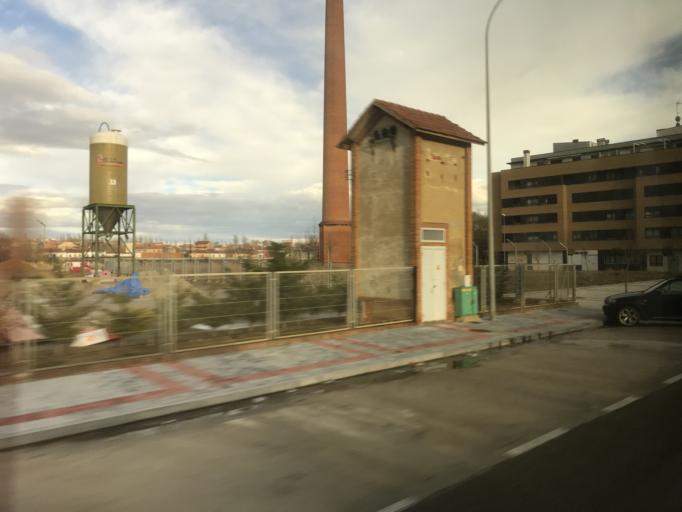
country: ES
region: Castille and Leon
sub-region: Provincia de Palencia
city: Palencia
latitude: 42.0212
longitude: -4.5445
